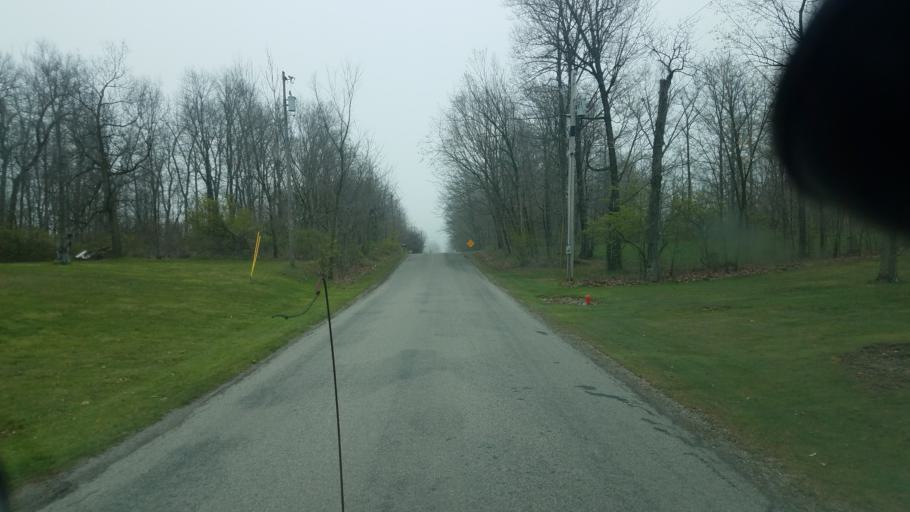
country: US
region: Ohio
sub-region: Logan County
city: Northwood
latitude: 40.4336
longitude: -83.7591
